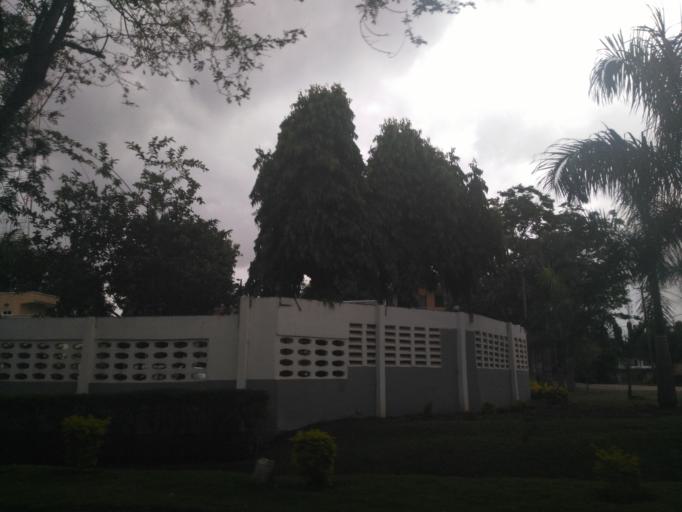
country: TZ
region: Dar es Salaam
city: Magomeni
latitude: -6.7933
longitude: 39.2730
